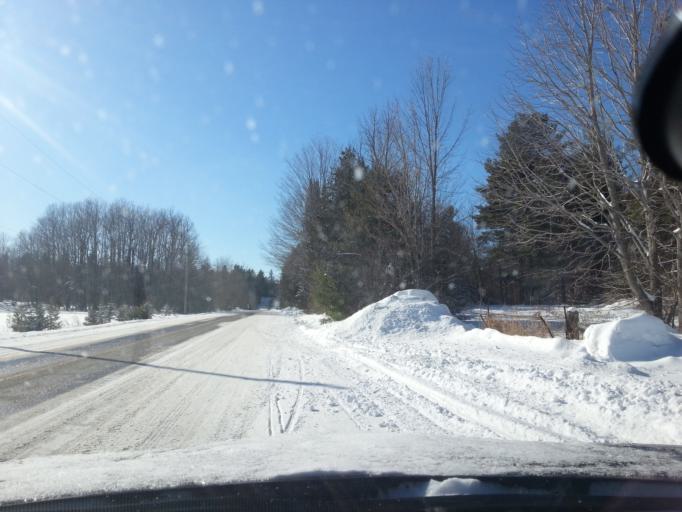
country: CA
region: Ontario
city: Arnprior
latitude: 45.2715
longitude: -76.3157
